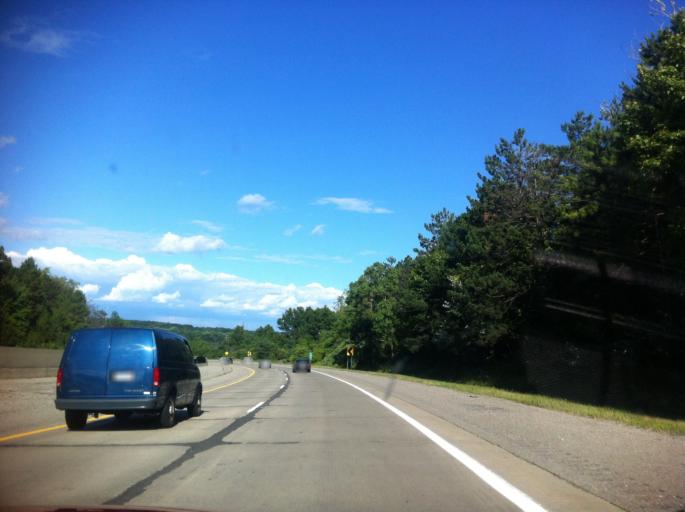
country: US
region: Michigan
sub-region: Washtenaw County
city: Ann Arbor
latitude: 42.2981
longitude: -83.7542
